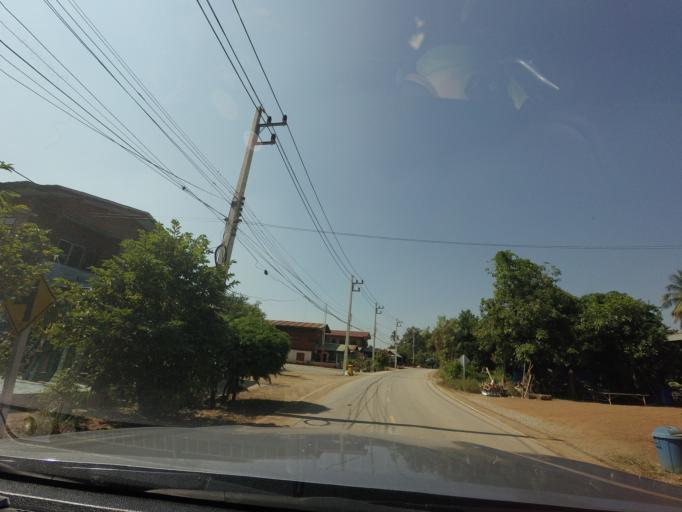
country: TH
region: Sukhothai
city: Si Samrong
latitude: 17.2181
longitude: 99.7771
